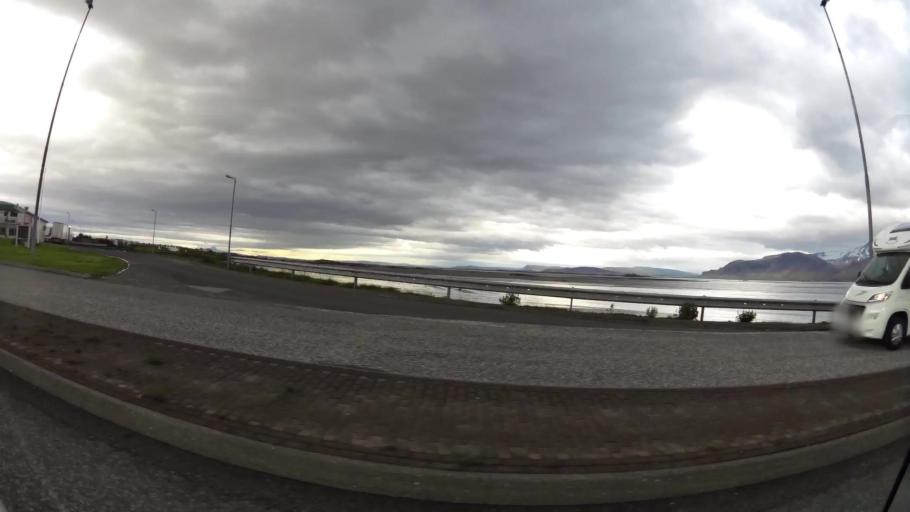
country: IS
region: West
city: Borgarnes
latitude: 64.5435
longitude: -21.9079
